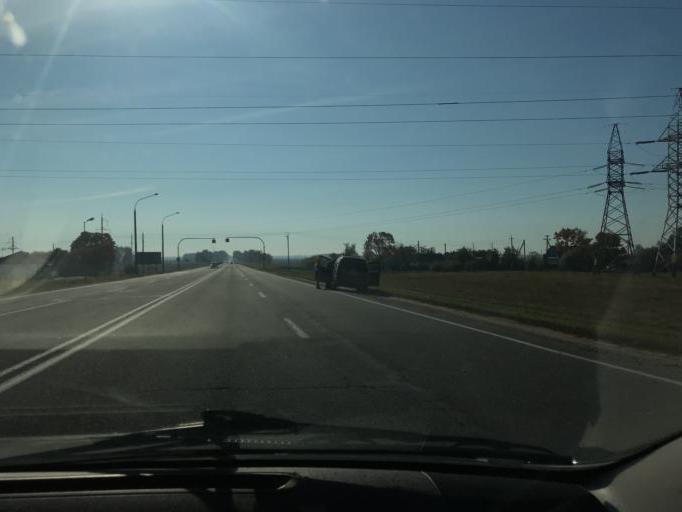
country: BY
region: Minsk
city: Salihorsk
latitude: 52.8521
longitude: 27.4664
